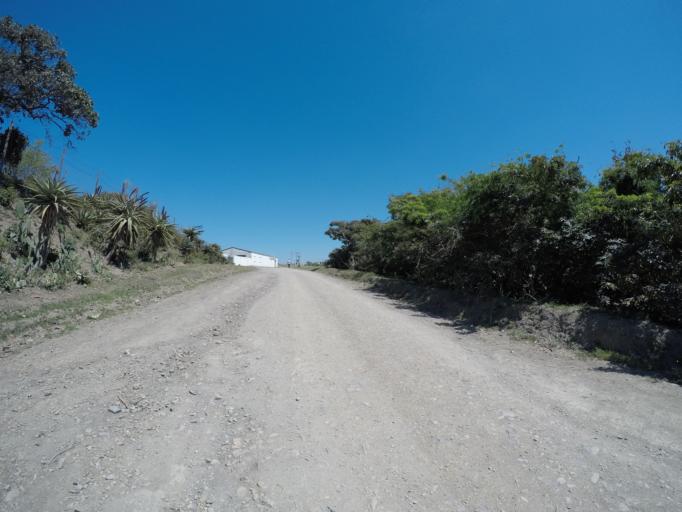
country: ZA
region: Eastern Cape
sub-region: OR Tambo District Municipality
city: Libode
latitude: -32.0317
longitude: 29.1104
